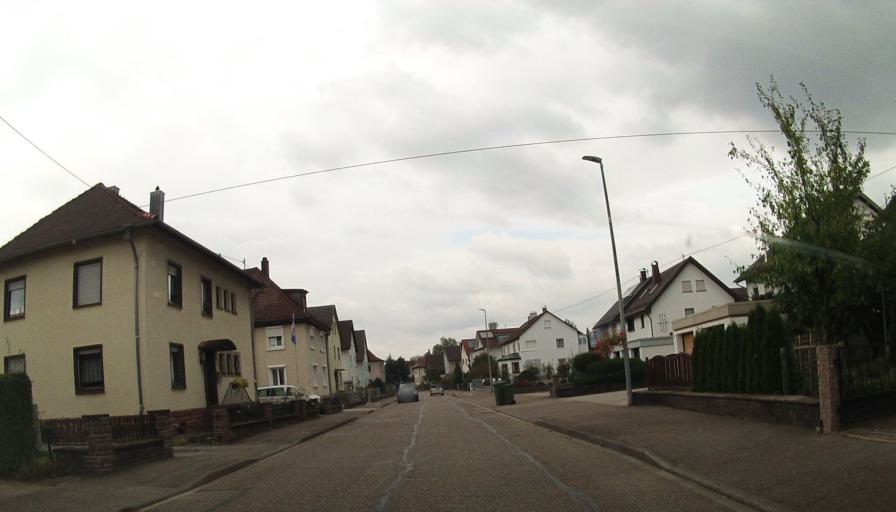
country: DE
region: Baden-Wuerttemberg
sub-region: Karlsruhe Region
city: Gaggenau
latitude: 48.8106
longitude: 8.3164
